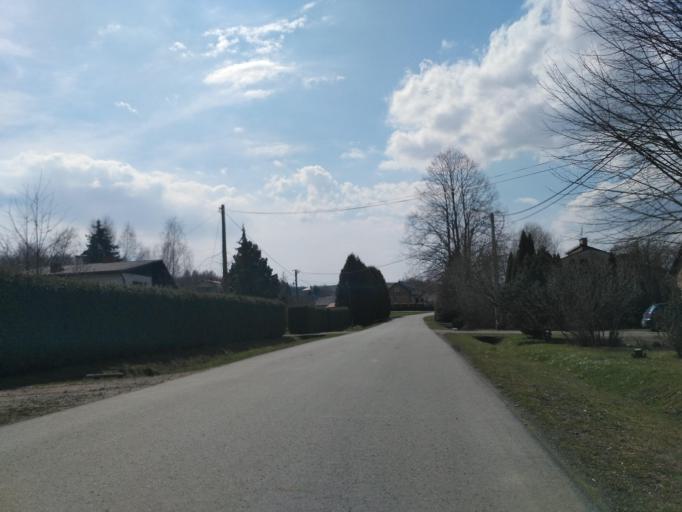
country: PL
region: Subcarpathian Voivodeship
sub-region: Powiat ropczycko-sedziszowski
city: Iwierzyce
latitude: 50.0035
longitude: 21.7610
